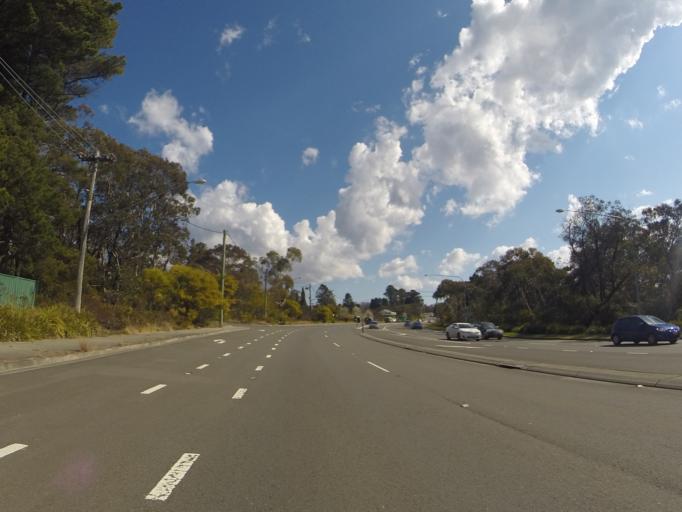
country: AU
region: New South Wales
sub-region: Blue Mountains Municipality
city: Leura
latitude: -33.7111
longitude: 150.3628
